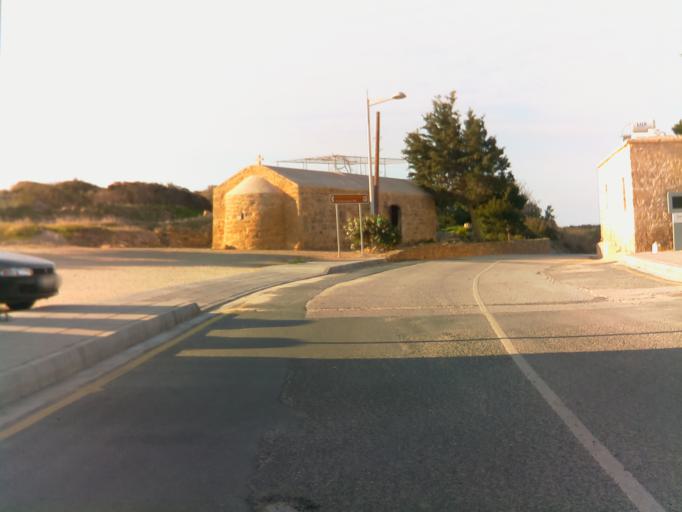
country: CY
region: Pafos
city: Pegeia
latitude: 34.9026
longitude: 32.3201
